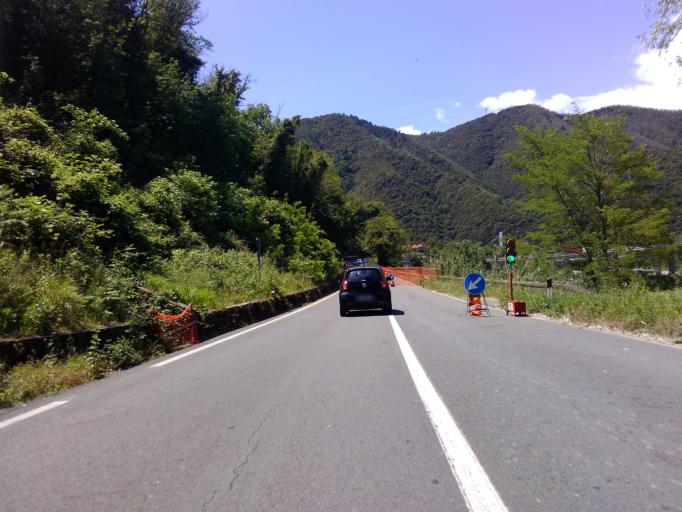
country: IT
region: Tuscany
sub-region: Provincia di Massa-Carrara
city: Albiano Magra
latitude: 44.1839
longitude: 9.9300
